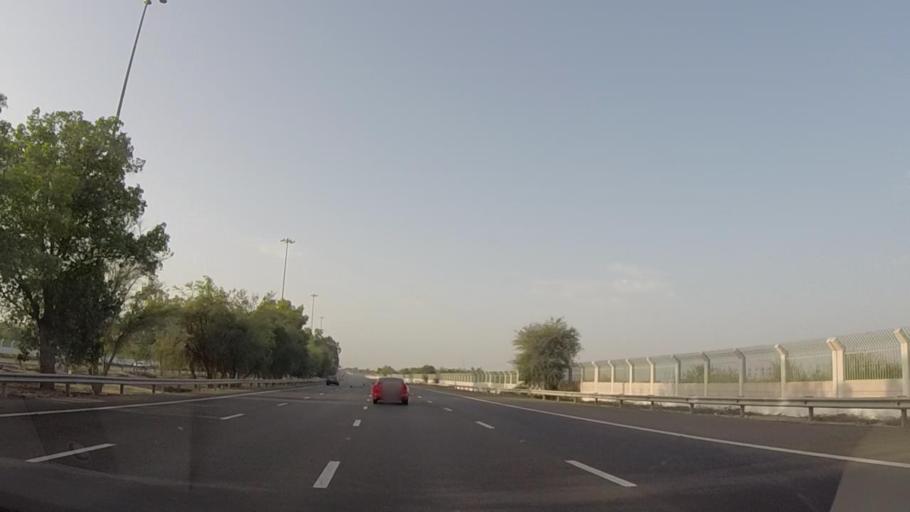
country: AE
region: Dubai
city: Dubai
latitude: 24.8140
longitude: 54.8711
